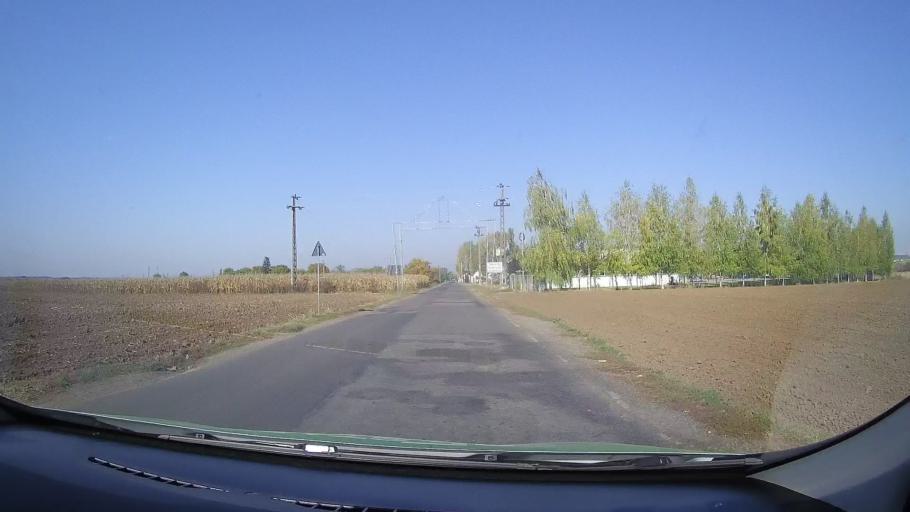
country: RO
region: Satu Mare
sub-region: Comuna Sanislau
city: Sanislau
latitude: 47.6279
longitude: 22.3366
